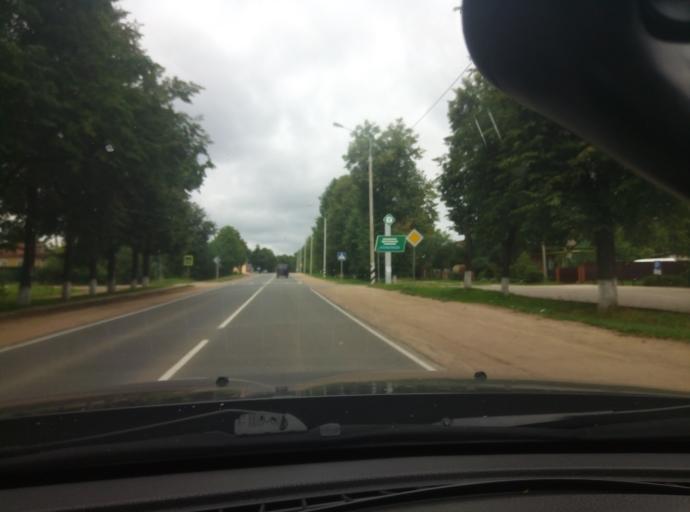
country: RU
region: Kaluga
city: Zhukovo
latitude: 55.0358
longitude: 36.7404
